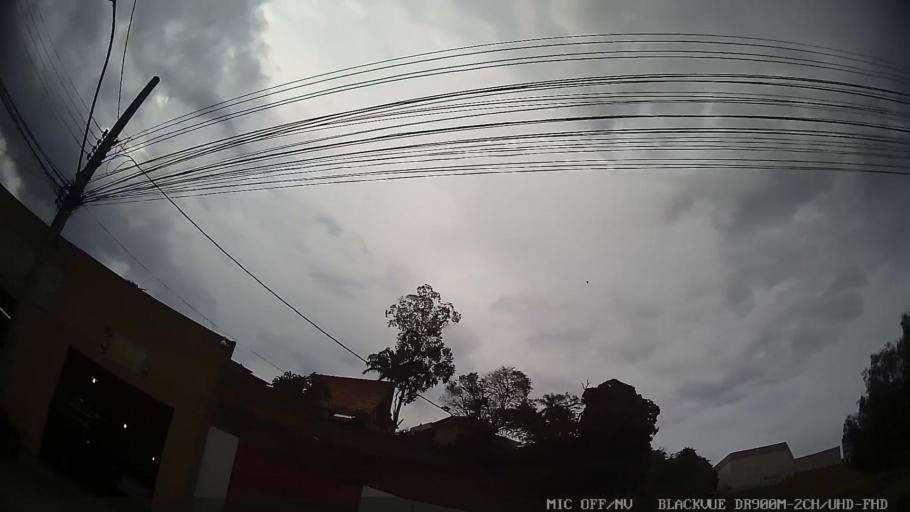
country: BR
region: Sao Paulo
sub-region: Itatiba
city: Itatiba
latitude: -23.0095
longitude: -46.8359
